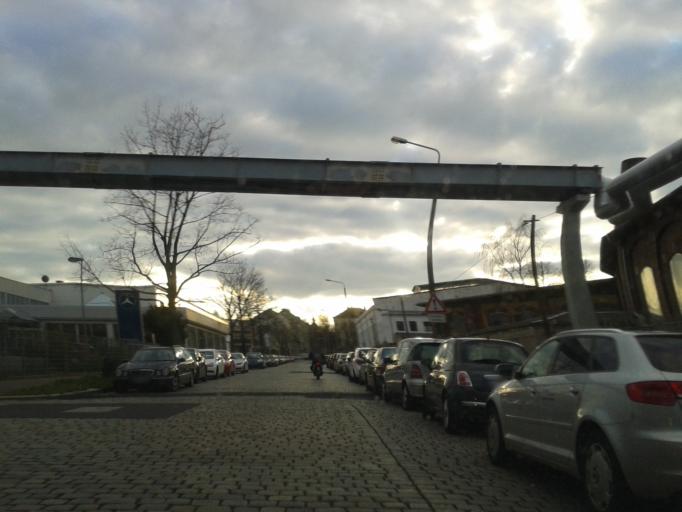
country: DE
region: Saxony
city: Dresden
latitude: 51.0354
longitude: 13.7097
